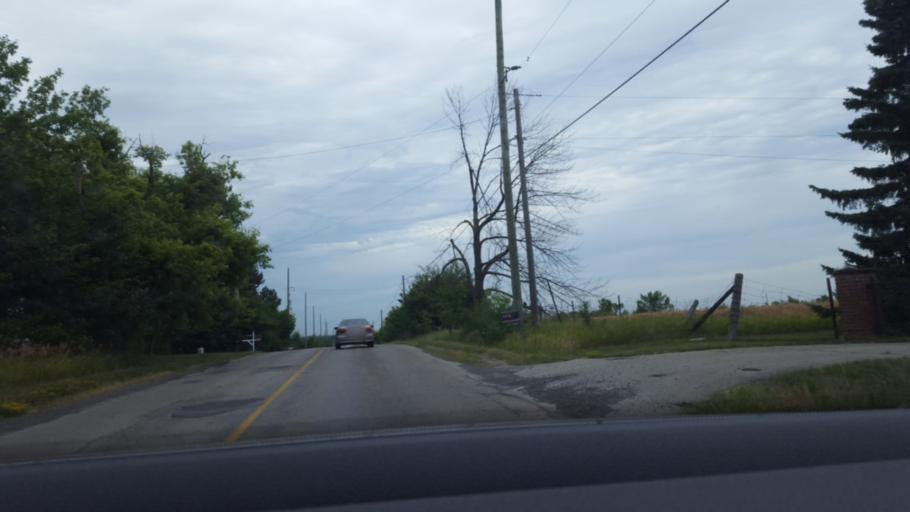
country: CA
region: Ontario
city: Brampton
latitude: 43.6149
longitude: -79.8389
